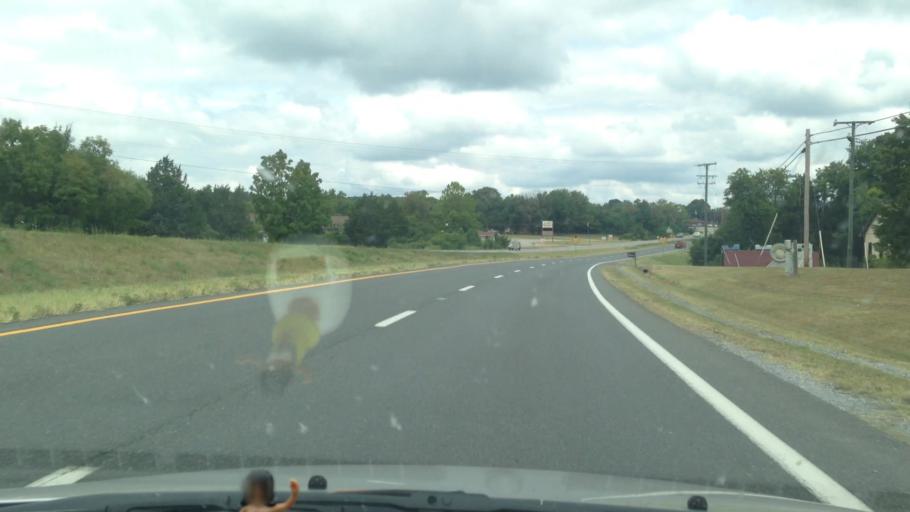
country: US
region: Virginia
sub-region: Campbell County
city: Rustburg
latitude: 37.2464
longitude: -79.1882
